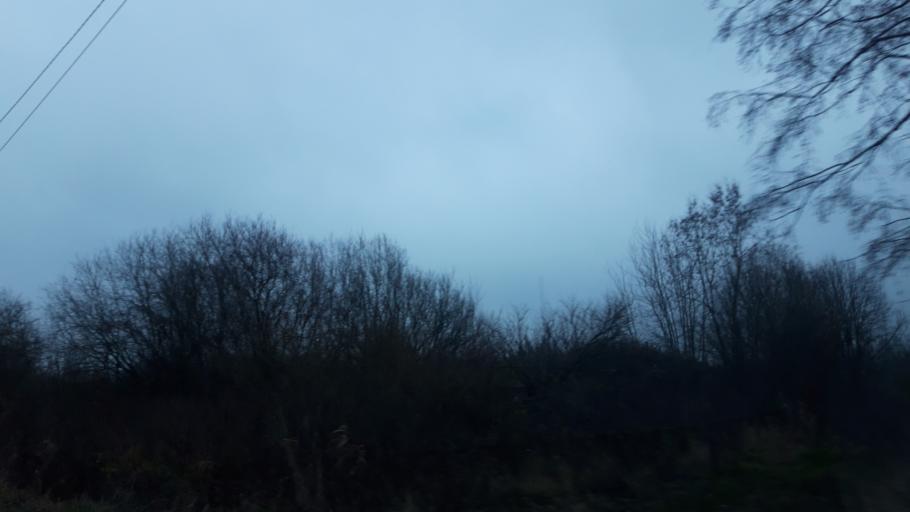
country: RU
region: Moskovskaya
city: Solnechnogorsk
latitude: 56.0788
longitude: 36.9216
